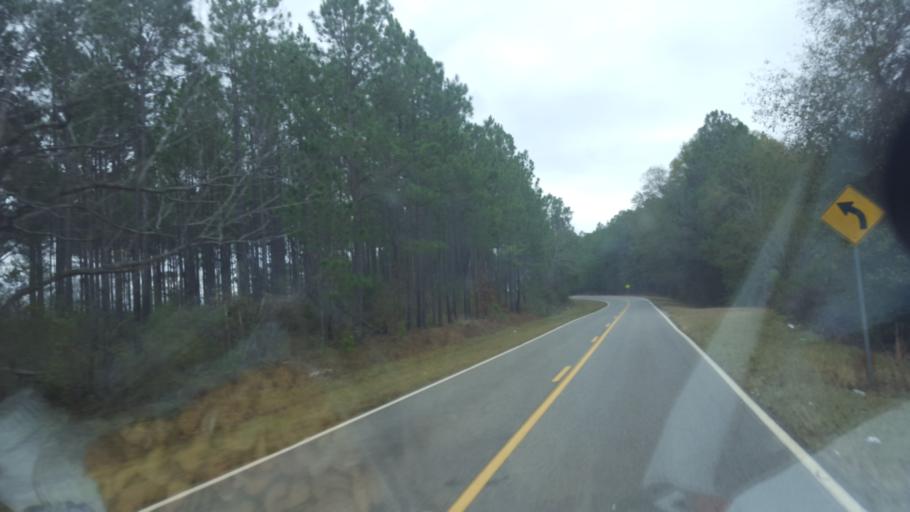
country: US
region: Georgia
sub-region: Wilcox County
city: Rochelle
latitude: 31.7863
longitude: -83.4345
